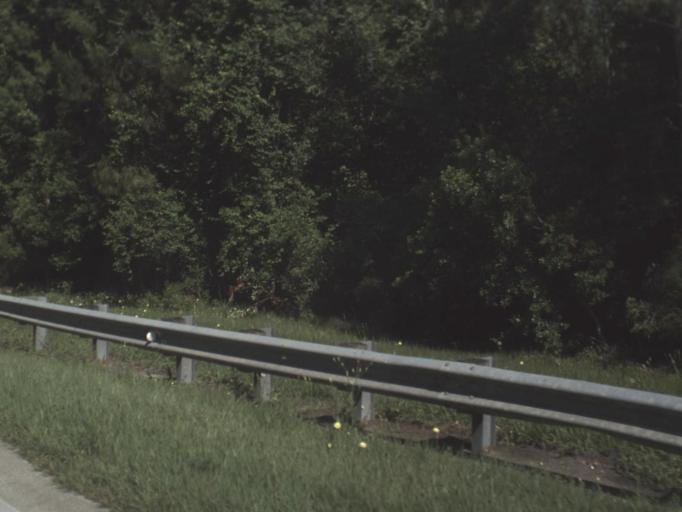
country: US
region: Florida
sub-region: Duval County
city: Baldwin
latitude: 30.3030
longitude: -81.9545
